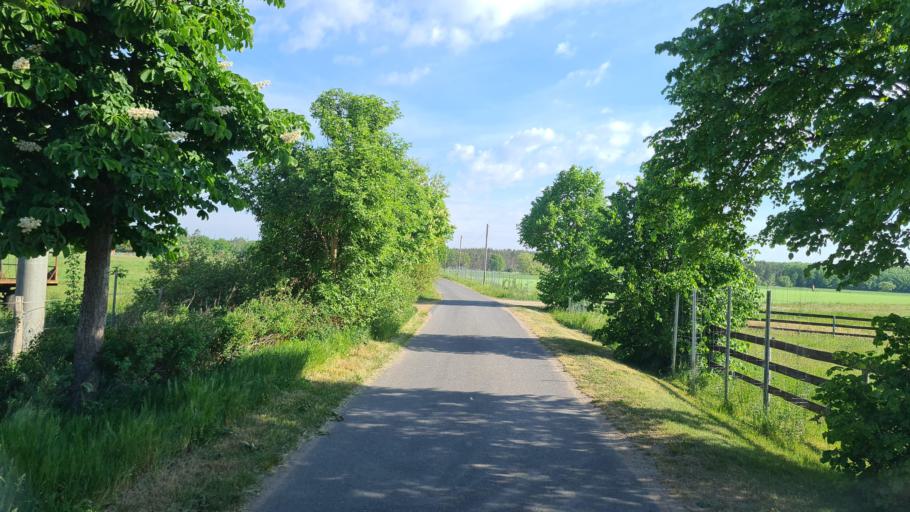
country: DE
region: Brandenburg
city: Falkenberg
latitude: 51.5883
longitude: 13.1749
